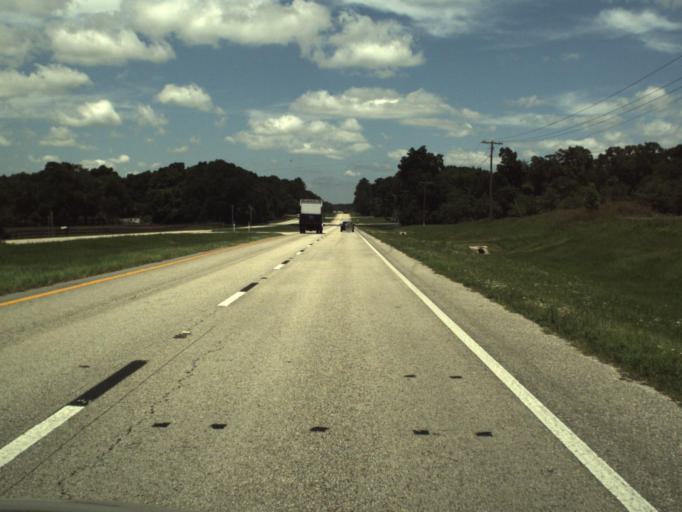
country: US
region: Florida
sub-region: Marion County
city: Citra
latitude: 29.3535
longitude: -82.1614
